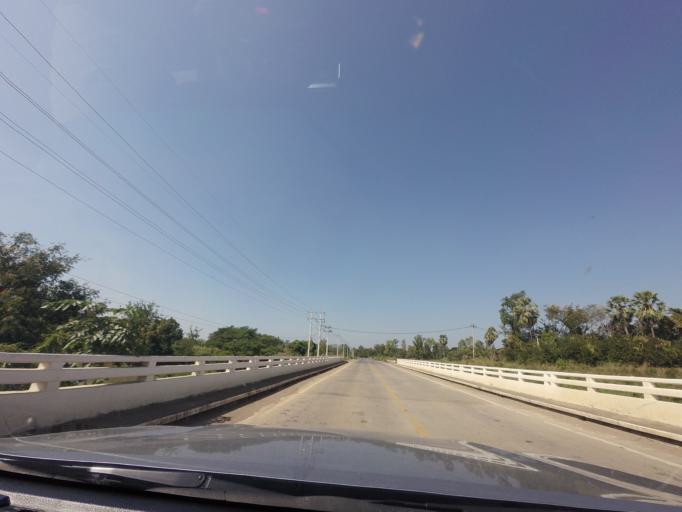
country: TH
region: Sukhothai
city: Sawankhalok
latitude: 17.3534
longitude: 99.8205
